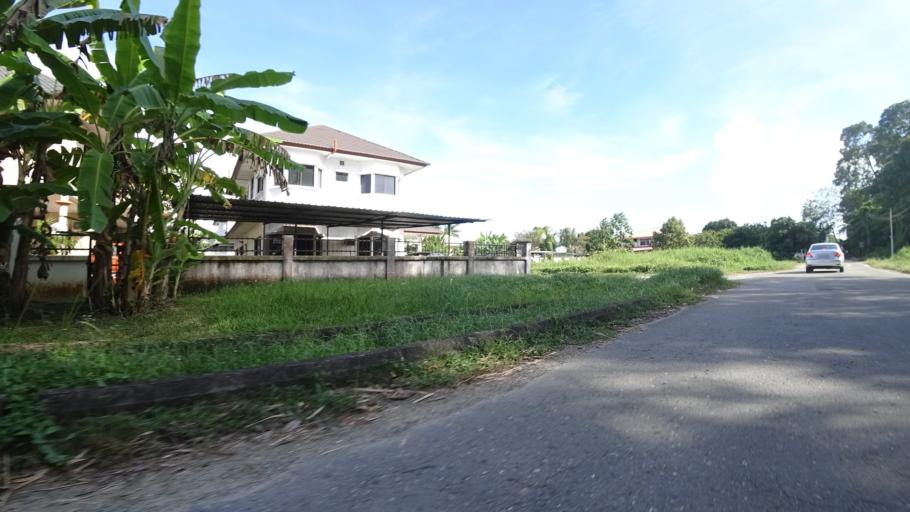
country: BN
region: Brunei and Muara
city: Bandar Seri Begawan
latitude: 4.9324
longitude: 114.8436
